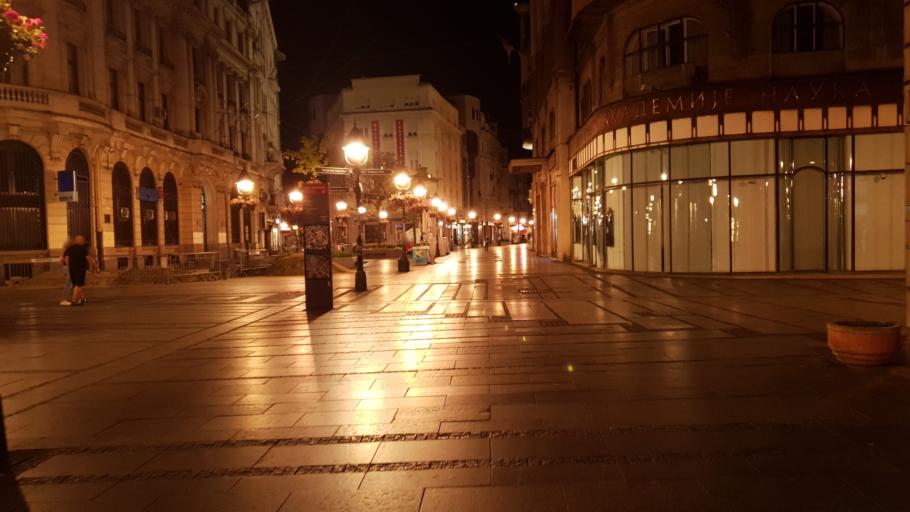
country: RS
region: Central Serbia
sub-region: Belgrade
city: Stari Grad
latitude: 44.8183
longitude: 20.4564
